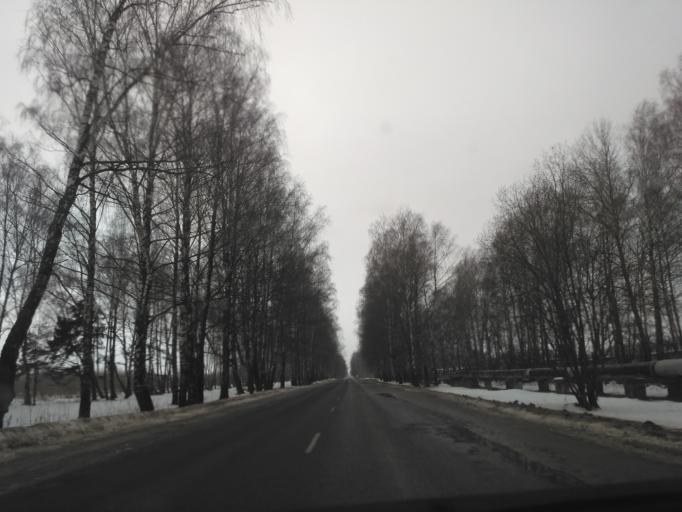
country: BY
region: Minsk
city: Horad Zhodzina
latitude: 54.0889
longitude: 28.3249
